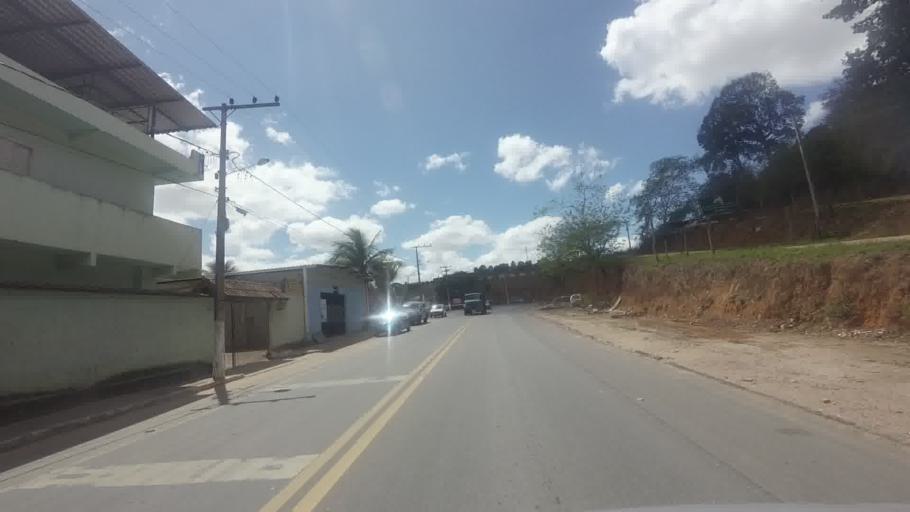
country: BR
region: Minas Gerais
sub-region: Recreio
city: Recreio
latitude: -21.6548
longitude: -42.3577
